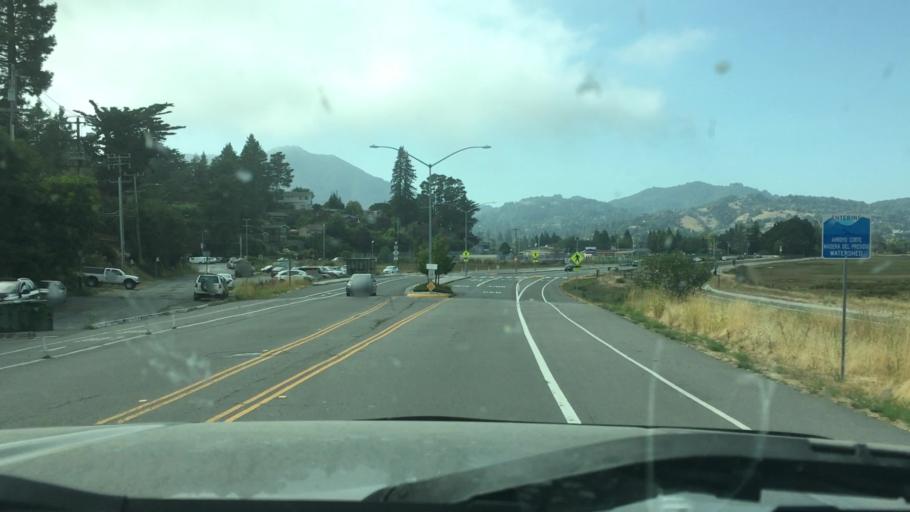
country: US
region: California
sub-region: Marin County
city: Tamalpais-Homestead Valley
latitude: 37.8864
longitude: -122.5240
